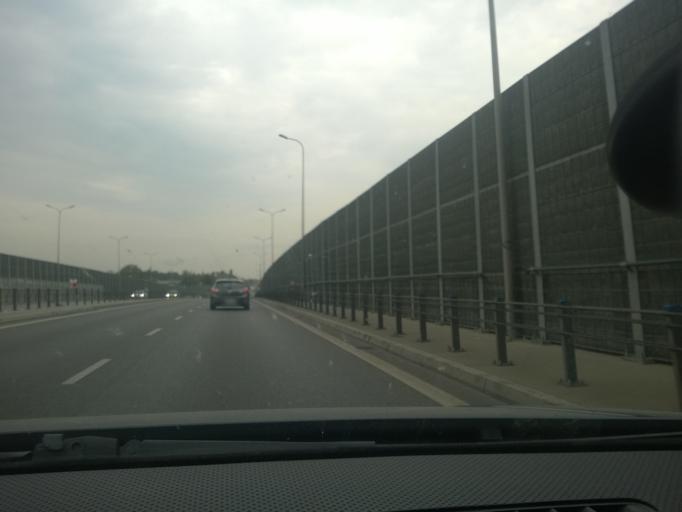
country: PL
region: Masovian Voivodeship
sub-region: Powiat warszawski zachodni
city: Lomianki
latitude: 52.3289
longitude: 20.9000
